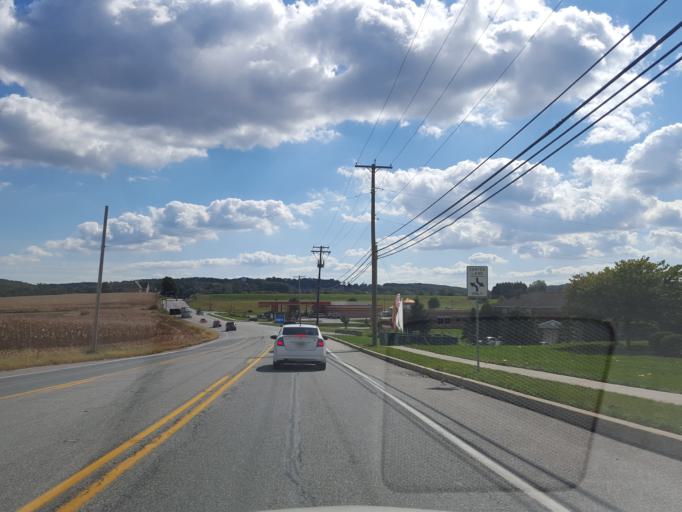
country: US
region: Pennsylvania
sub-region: York County
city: Stonybrook
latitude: 39.9480
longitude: -76.6480
